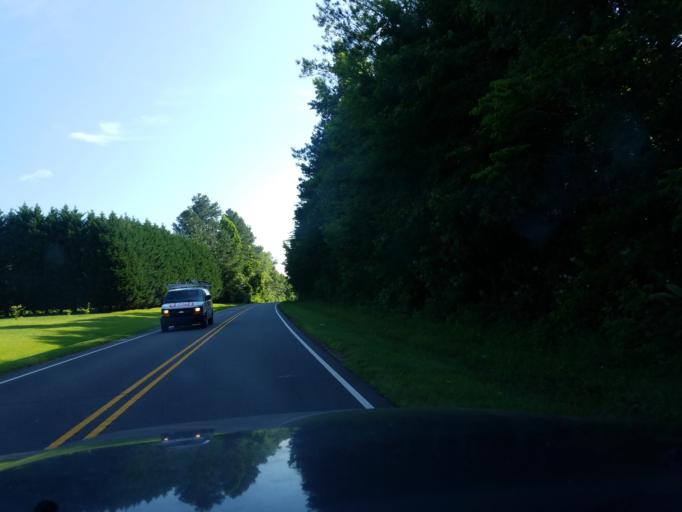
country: US
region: North Carolina
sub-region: Granville County
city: Creedmoor
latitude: 36.2425
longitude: -78.6944
